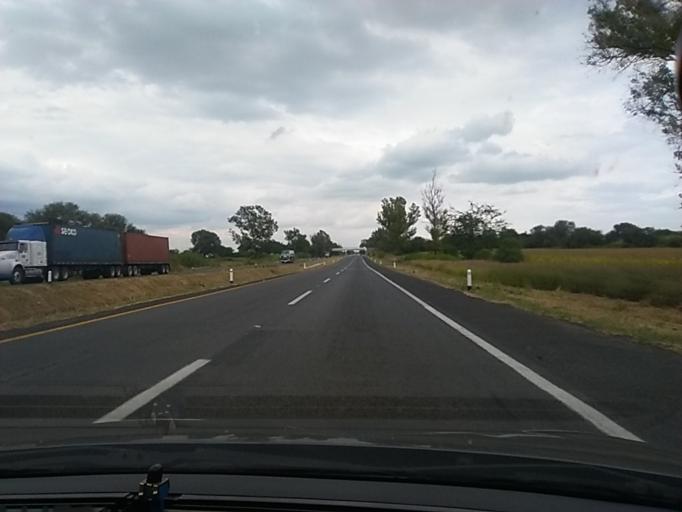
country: MX
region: Jalisco
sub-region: Ocotlan
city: Joconoxtle (La Tuna)
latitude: 20.3806
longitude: -102.6960
